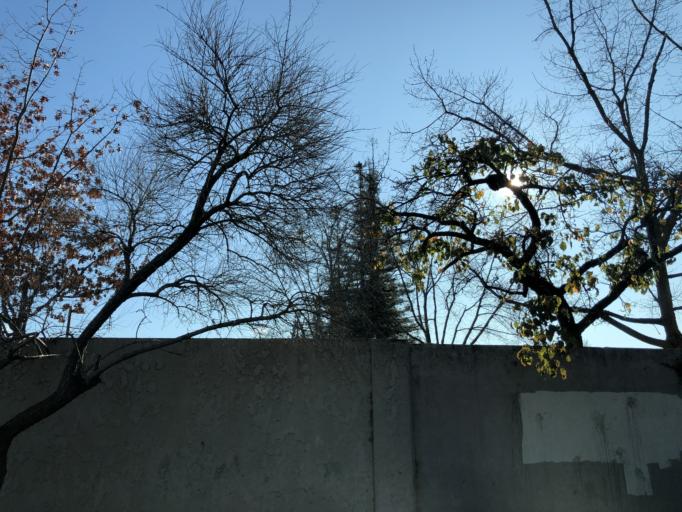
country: US
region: California
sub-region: Sacramento County
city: Rosemont
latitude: 38.5504
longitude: -121.4056
